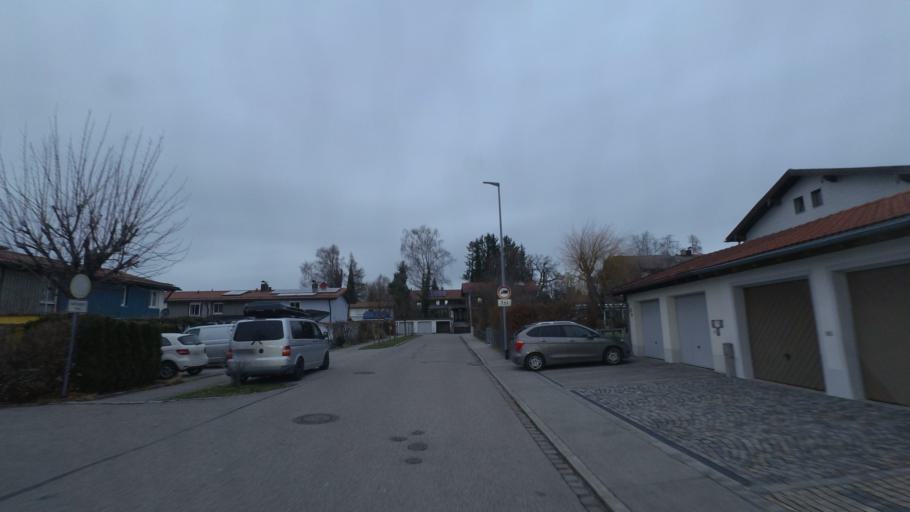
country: DE
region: Bavaria
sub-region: Upper Bavaria
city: Traunstein
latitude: 47.8687
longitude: 12.6267
